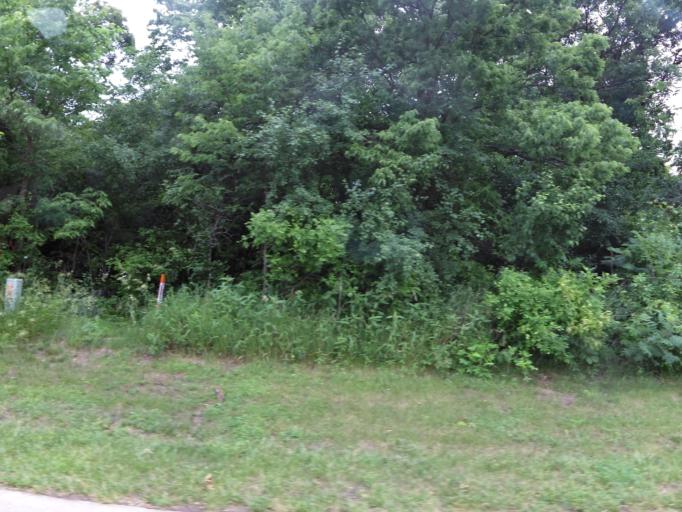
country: US
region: Minnesota
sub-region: Scott County
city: Prior Lake
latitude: 44.7561
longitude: -93.4558
